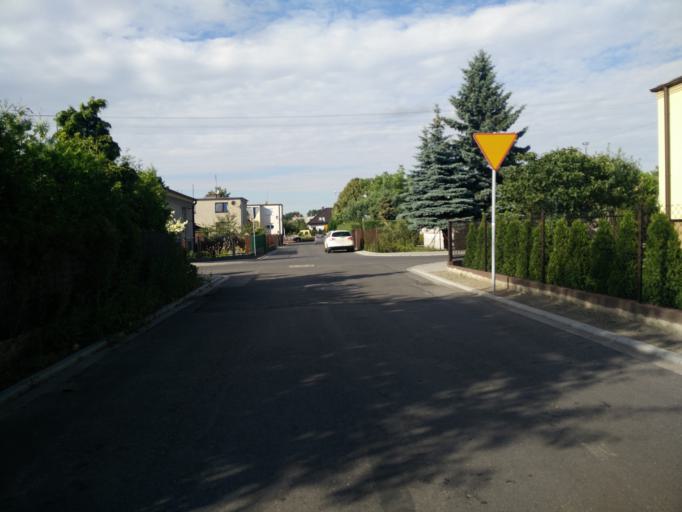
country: PL
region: Greater Poland Voivodeship
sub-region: Powiat sredzki
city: Sroda Wielkopolska
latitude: 52.2345
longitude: 17.2567
